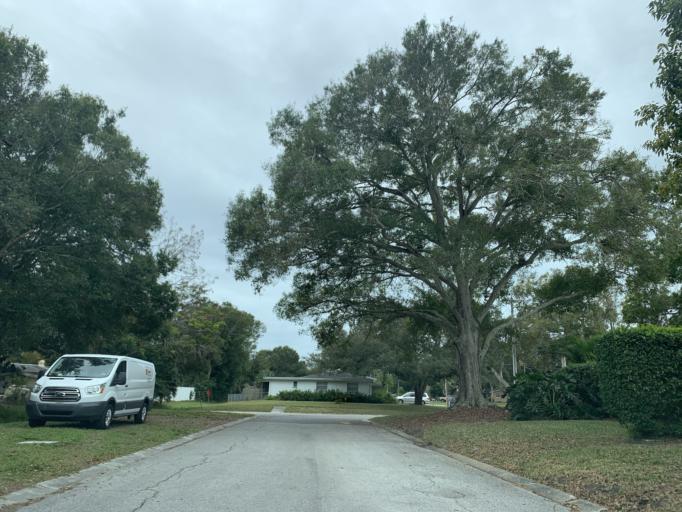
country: US
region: Florida
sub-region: Pinellas County
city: Belleair
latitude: 27.9356
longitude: -82.7793
